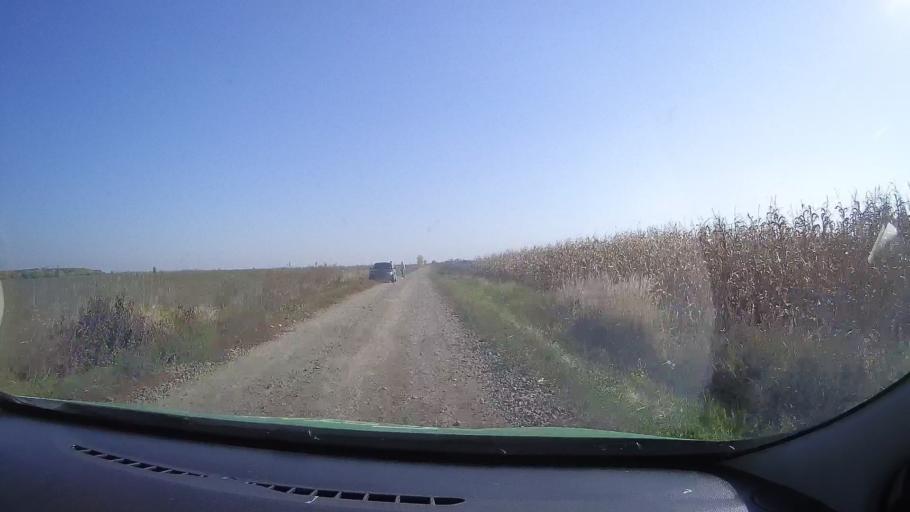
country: RO
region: Satu Mare
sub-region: Comuna Urziceni
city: Urziceni
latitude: 47.7358
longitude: 22.4235
